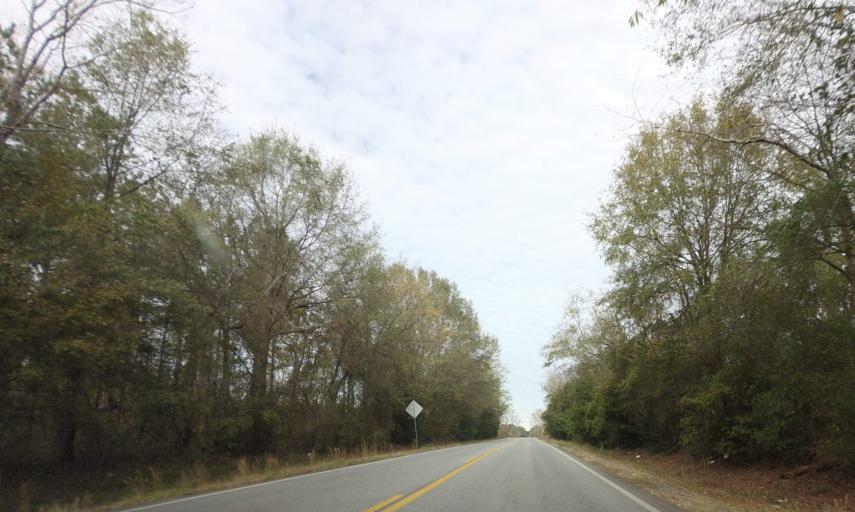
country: US
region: Georgia
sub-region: Dodge County
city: Chester
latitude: 32.5072
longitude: -83.0929
